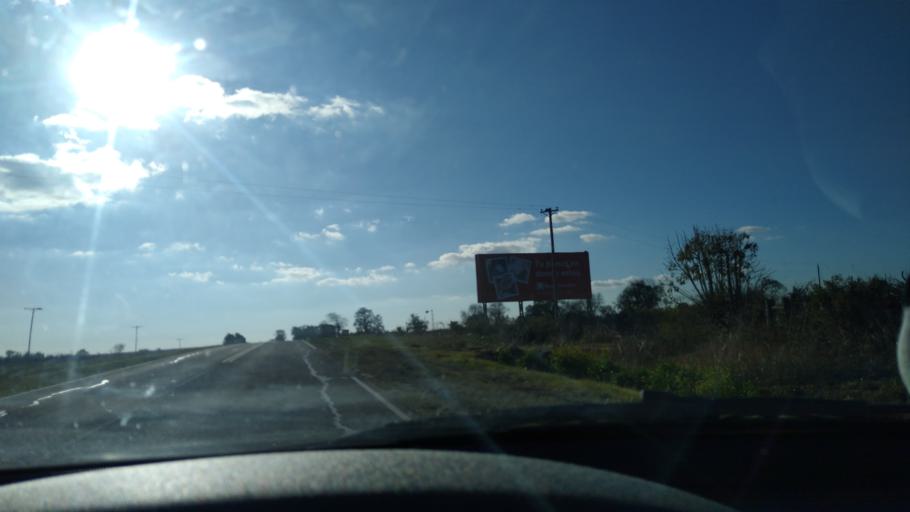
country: AR
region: Entre Rios
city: Diamante
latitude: -32.1084
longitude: -60.5789
